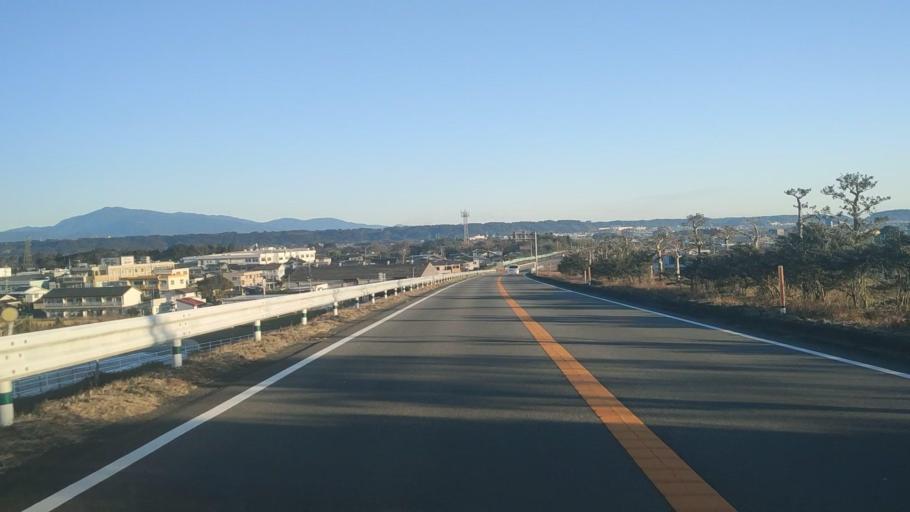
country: JP
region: Miyazaki
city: Tsuma
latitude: 32.0338
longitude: 131.4653
